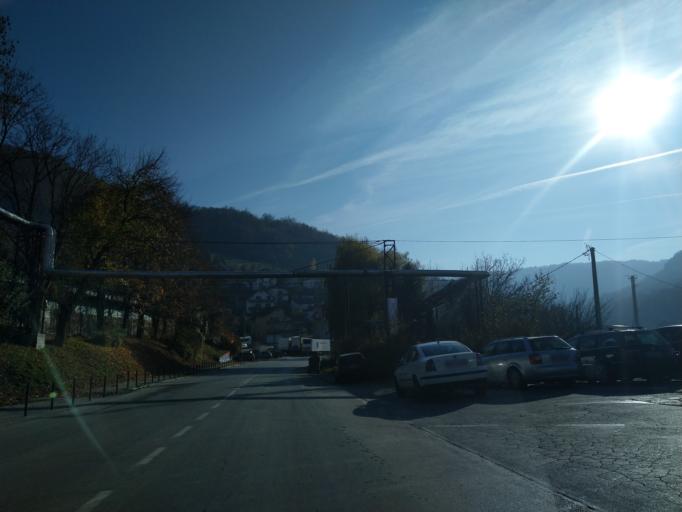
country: RS
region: Central Serbia
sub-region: Zlatiborski Okrug
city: Uzice
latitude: 43.8469
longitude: 19.8631
